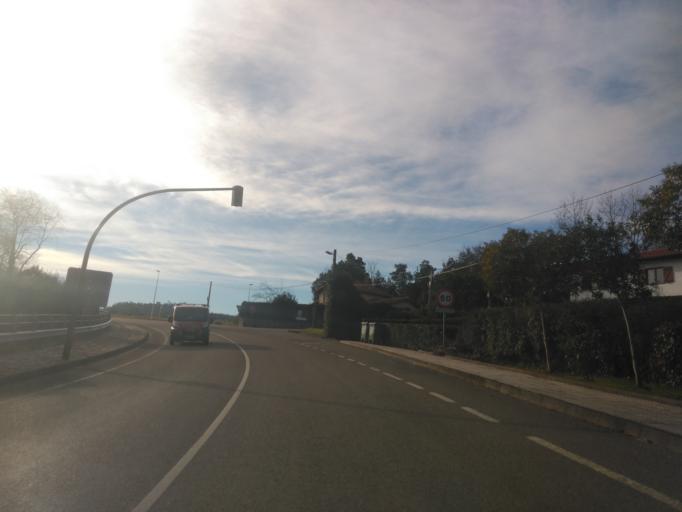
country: ES
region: Cantabria
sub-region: Provincia de Cantabria
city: Comillas
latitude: 43.3794
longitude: -4.2900
